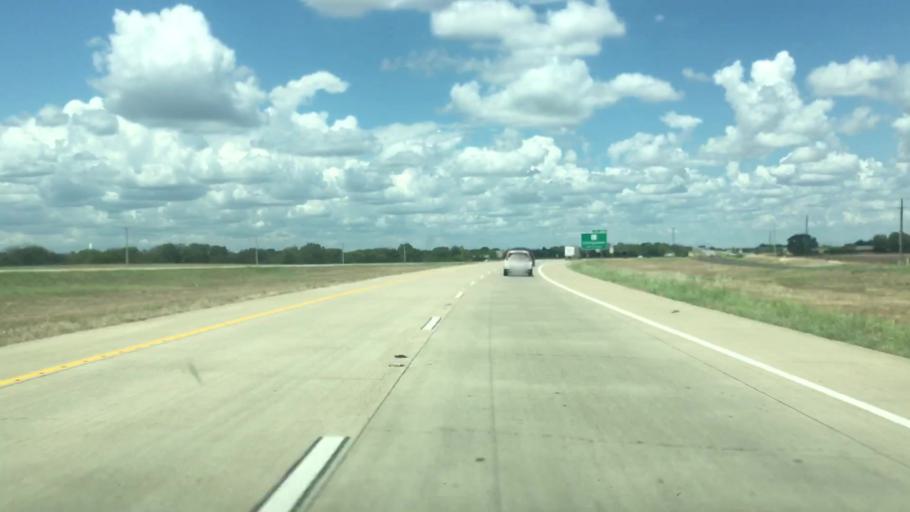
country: US
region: Texas
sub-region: Williamson County
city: Georgetown
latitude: 30.6281
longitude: -97.6259
